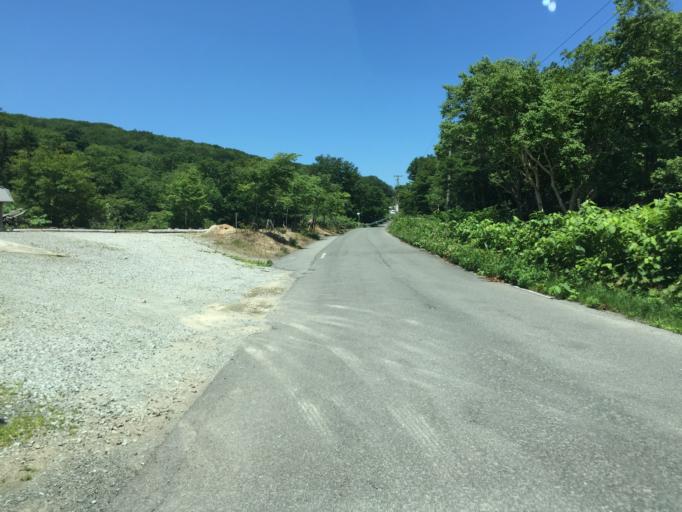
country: JP
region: Fukushima
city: Inawashiro
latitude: 37.6689
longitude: 140.2695
